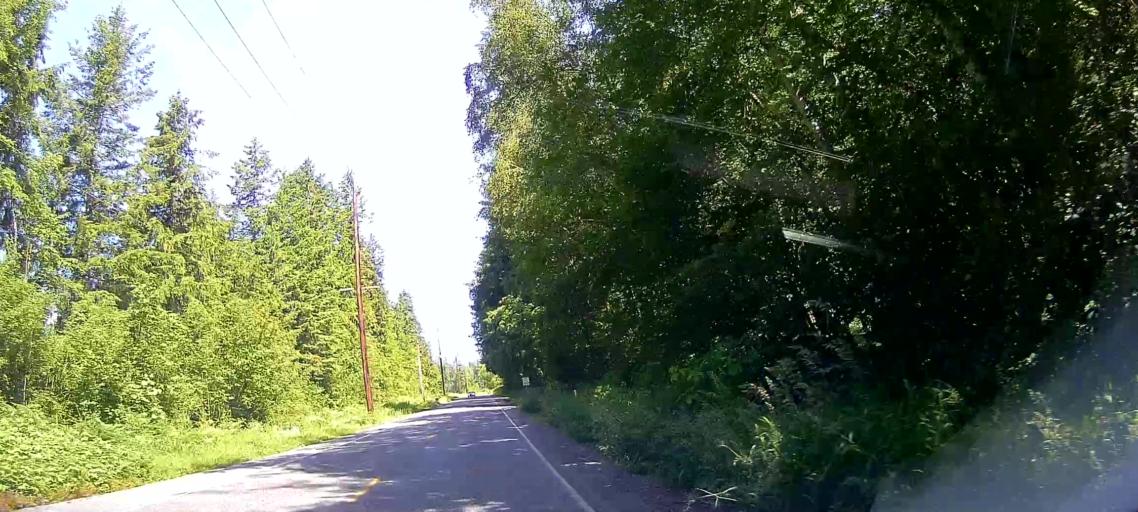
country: US
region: Washington
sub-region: Skagit County
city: Burlington
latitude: 48.5385
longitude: -122.3108
